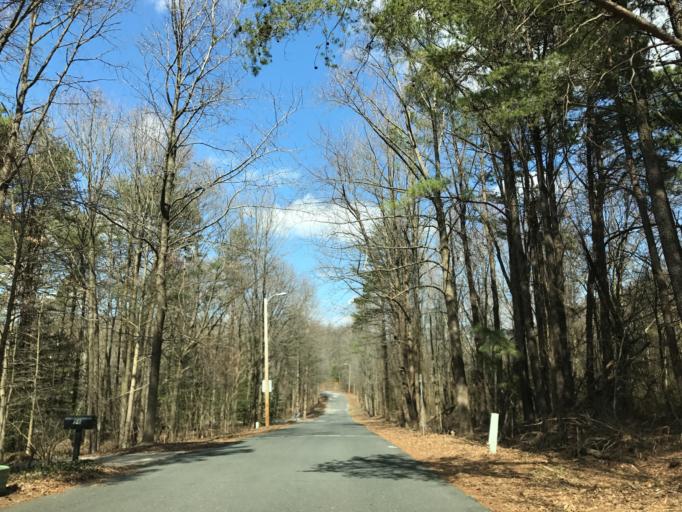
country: US
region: Maryland
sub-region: Anne Arundel County
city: Green Haven
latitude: 39.1145
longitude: -76.5233
